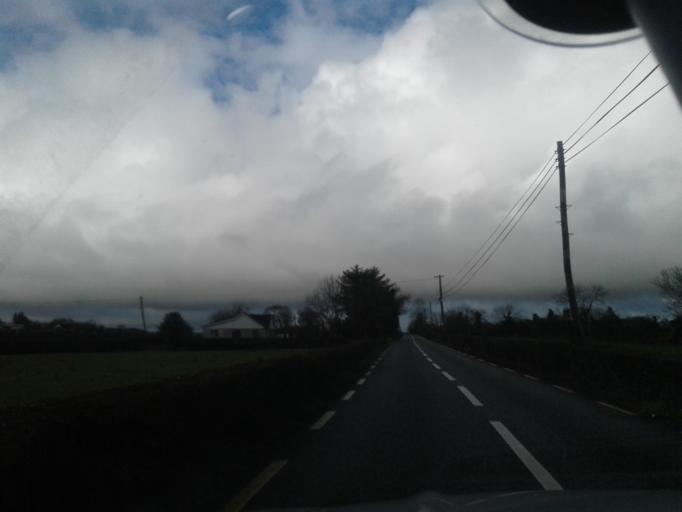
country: IE
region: Ulster
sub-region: County Donegal
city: Ramelton
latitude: 55.0647
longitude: -7.6096
